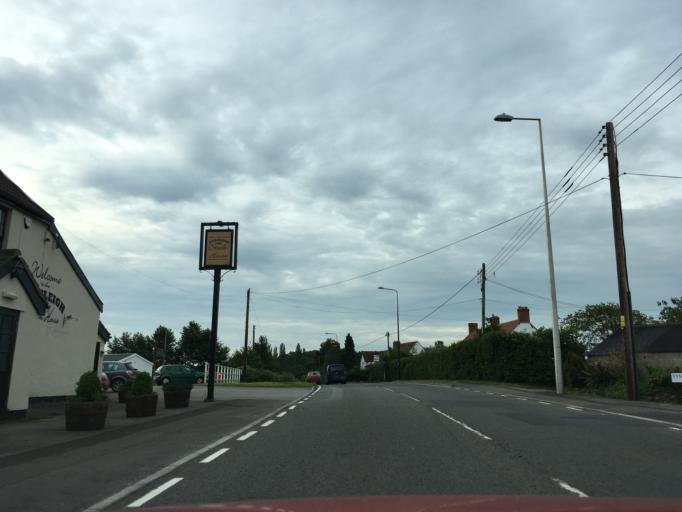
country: GB
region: England
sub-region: North Somerset
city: Easton-in-Gordano
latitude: 51.4726
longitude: -2.6956
